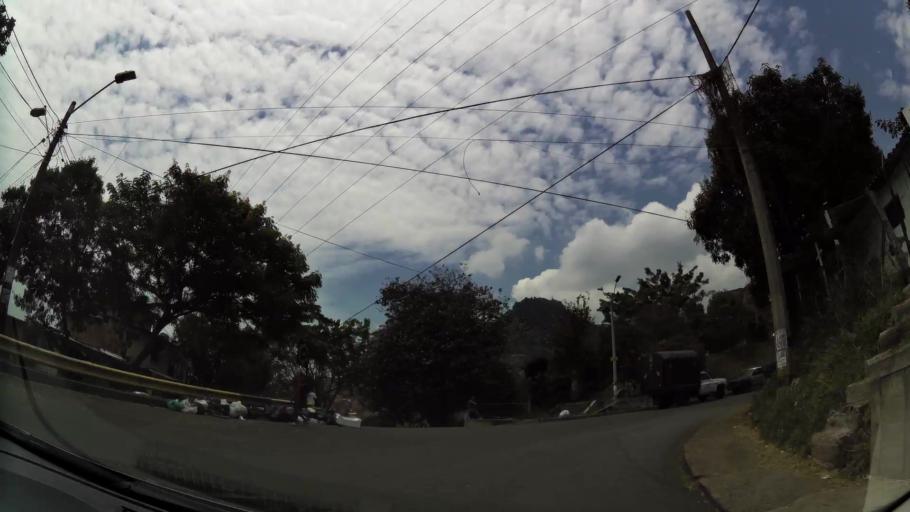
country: CO
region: Antioquia
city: Bello
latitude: 6.3063
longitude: -75.5779
